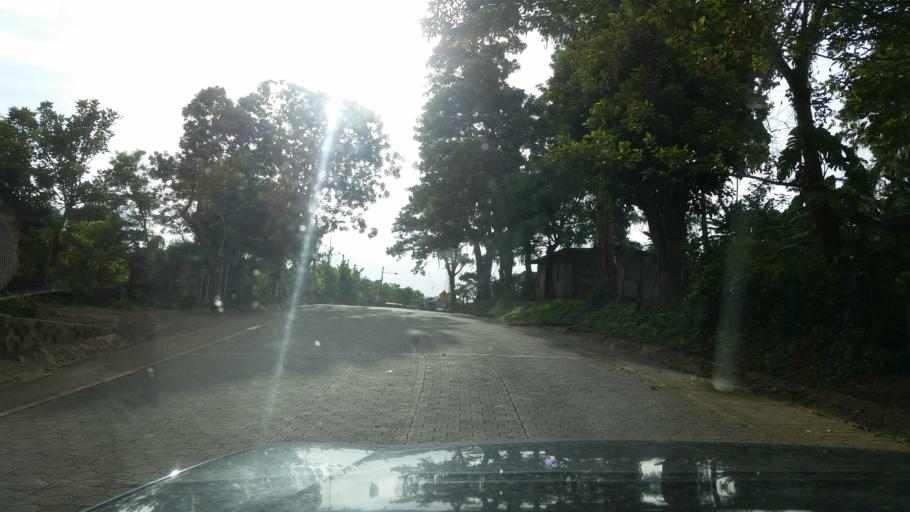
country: NI
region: Matagalpa
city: San Ramon
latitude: 13.1465
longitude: -85.7353
